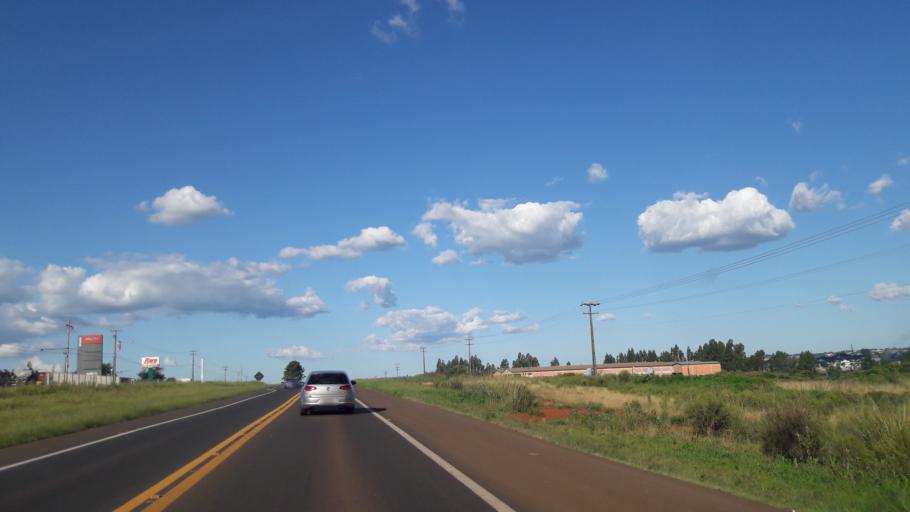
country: BR
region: Parana
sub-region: Guarapuava
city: Guarapuava
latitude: -25.3828
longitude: -51.5115
